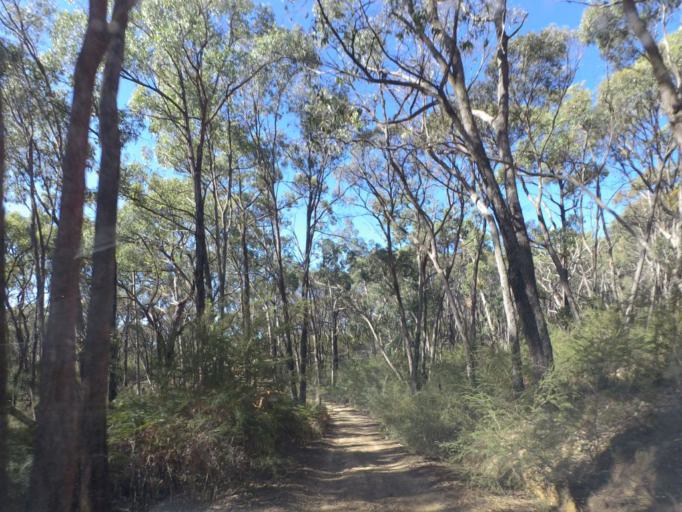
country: AU
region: Victoria
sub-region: Murrindindi
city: Kinglake West
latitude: -37.4684
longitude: 145.3645
